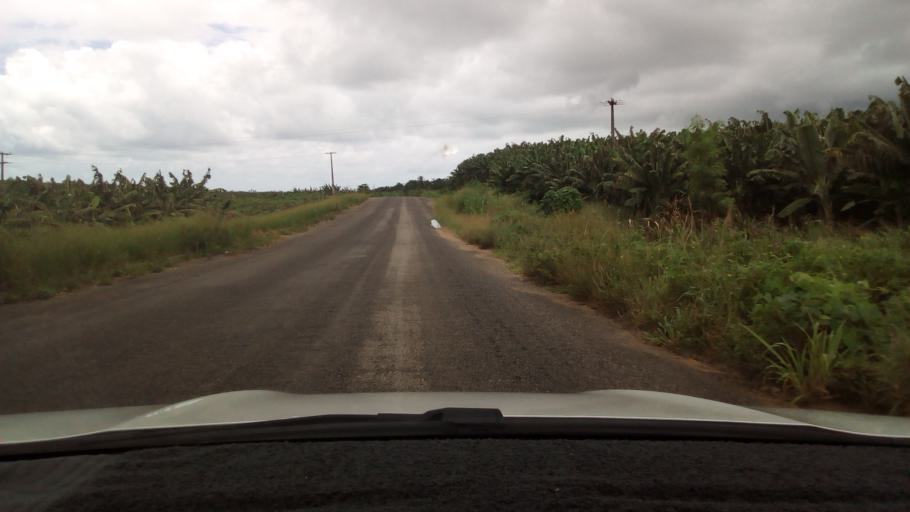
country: BR
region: Paraiba
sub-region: Pitimbu
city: Pitimbu
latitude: -7.3567
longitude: -34.8208
